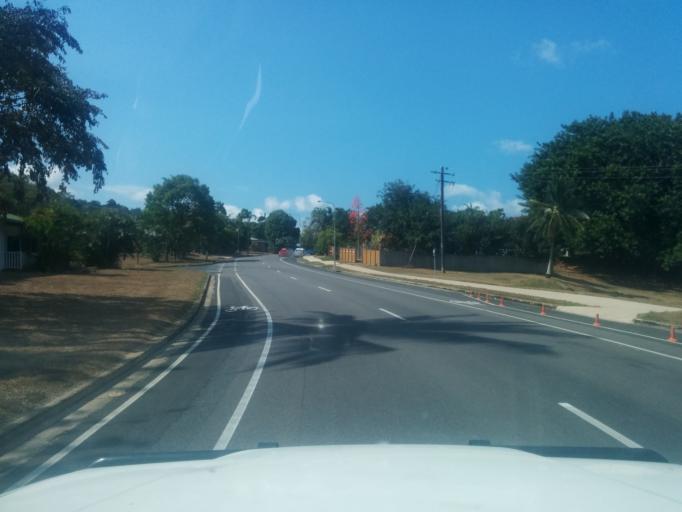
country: AU
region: Queensland
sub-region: Cairns
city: Woree
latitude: -16.9423
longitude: 145.7287
